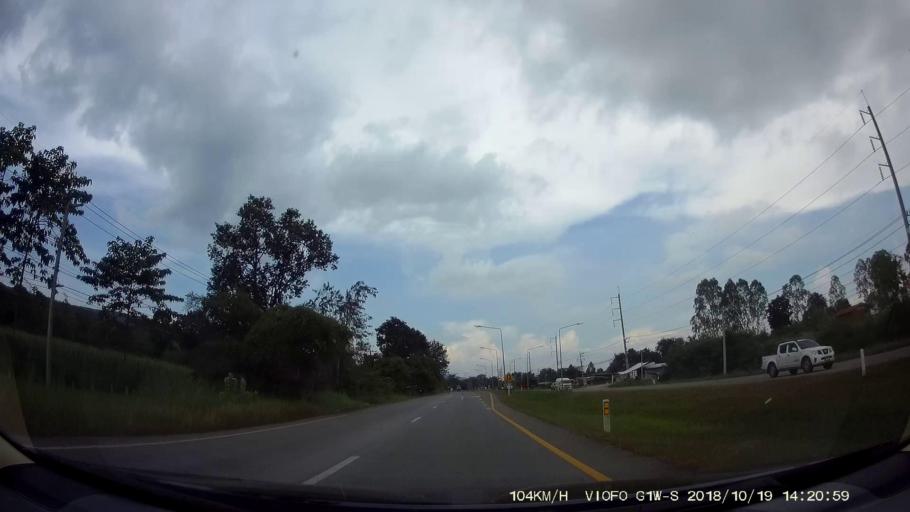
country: TH
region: Chaiyaphum
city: Kaeng Khro
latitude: 16.0472
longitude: 102.2615
